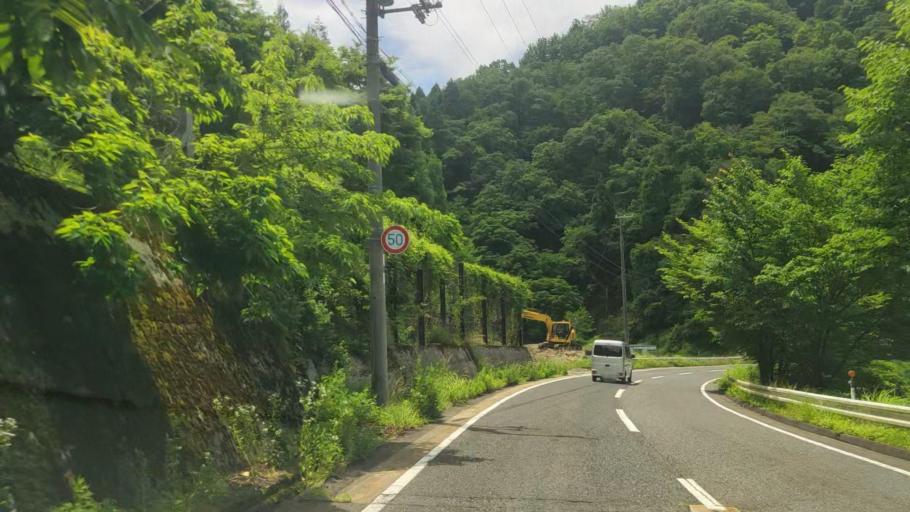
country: JP
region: Hyogo
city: Toyooka
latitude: 35.4806
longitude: 134.6126
